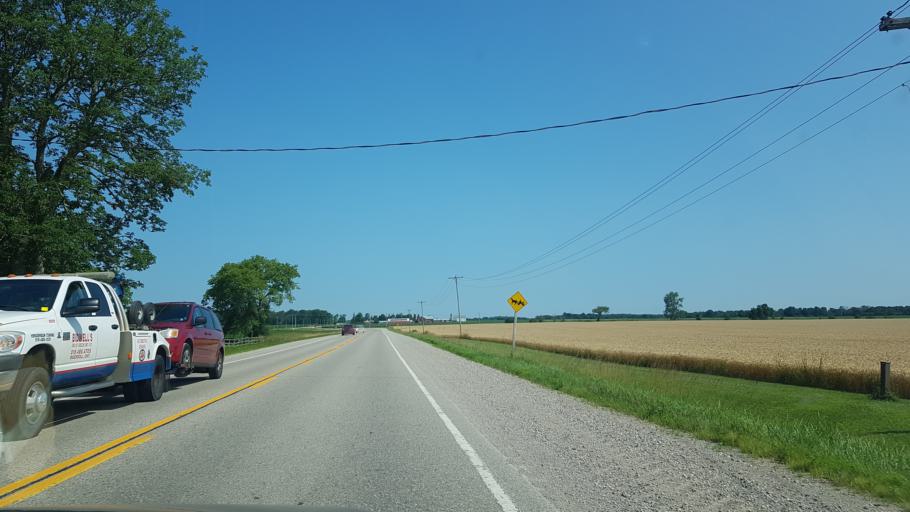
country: CA
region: Ontario
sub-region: Oxford County
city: Woodstock
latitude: 42.9263
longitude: -80.6732
